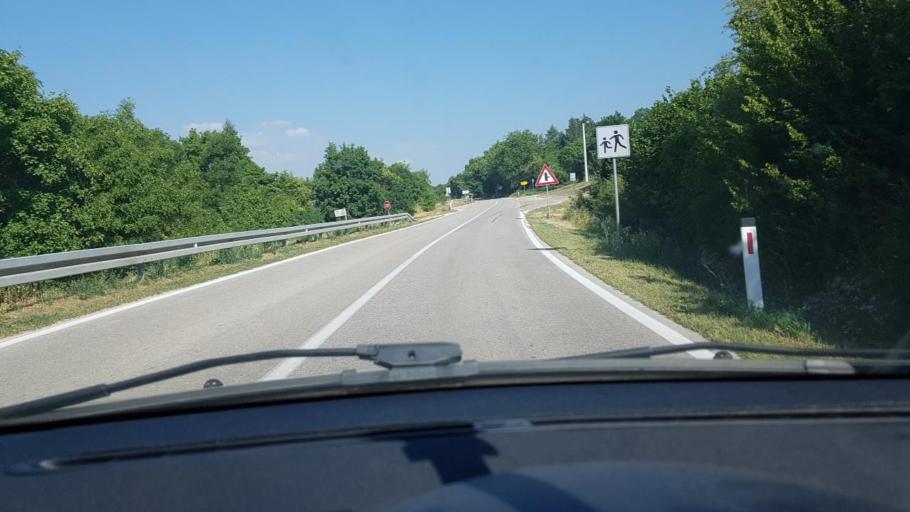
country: BA
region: Federation of Bosnia and Herzegovina
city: Bila
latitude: 43.8655
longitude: 16.8855
